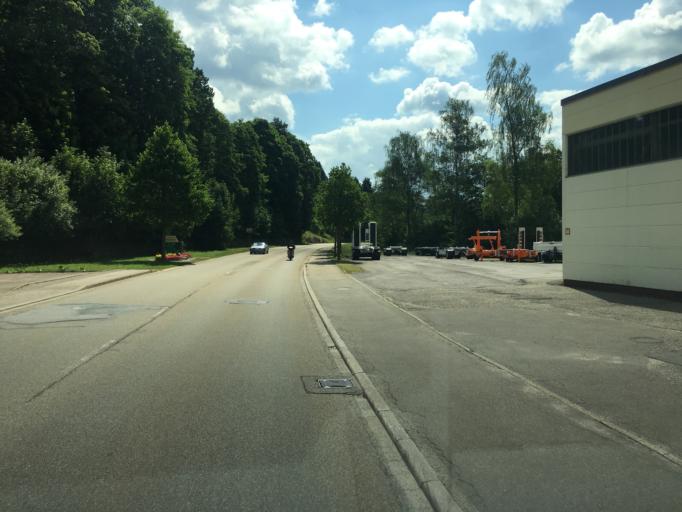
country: DE
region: Baden-Wuerttemberg
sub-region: Karlsruhe Region
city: Baiersbronn
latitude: 48.5193
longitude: 8.3322
